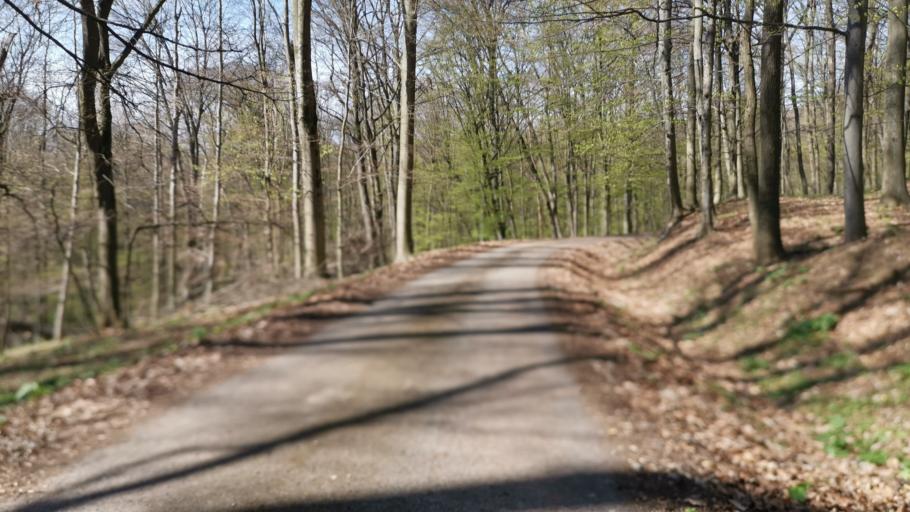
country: SK
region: Trnavsky
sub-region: Okres Skalica
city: Skalica
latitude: 48.7346
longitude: 17.2471
